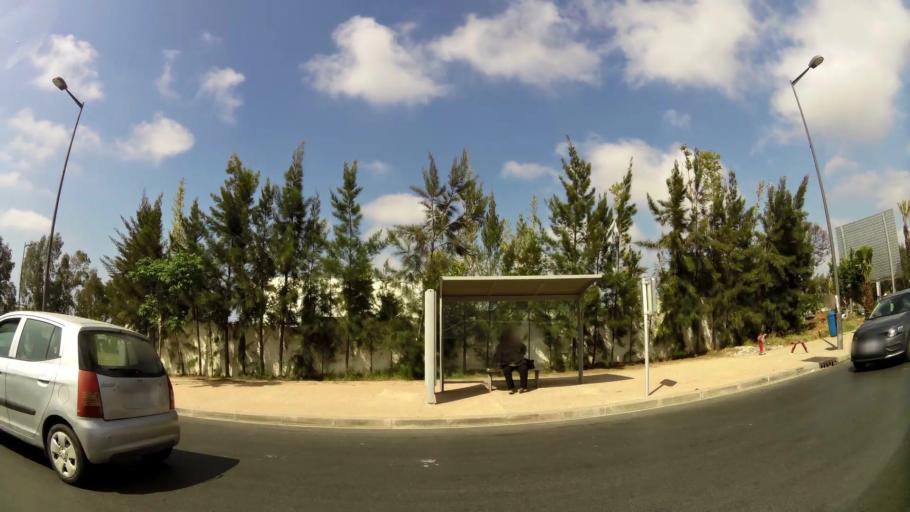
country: MA
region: Rabat-Sale-Zemmour-Zaer
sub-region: Rabat
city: Rabat
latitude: 33.9704
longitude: -6.8668
